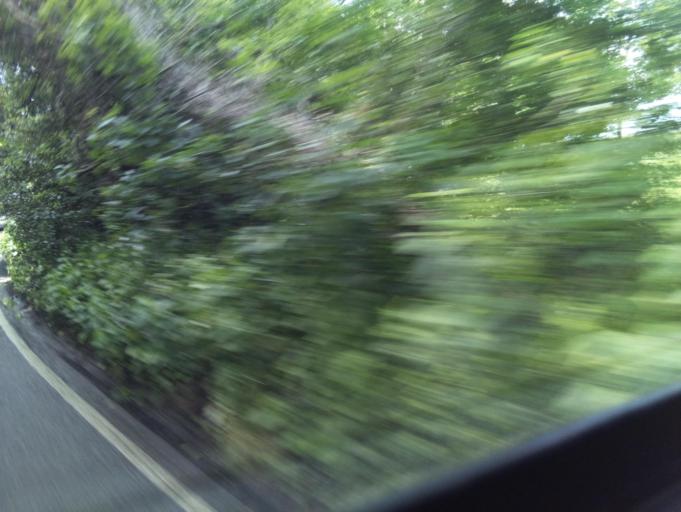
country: GB
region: England
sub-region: Hertfordshire
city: Kings Langley
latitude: 51.6741
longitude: -0.4432
